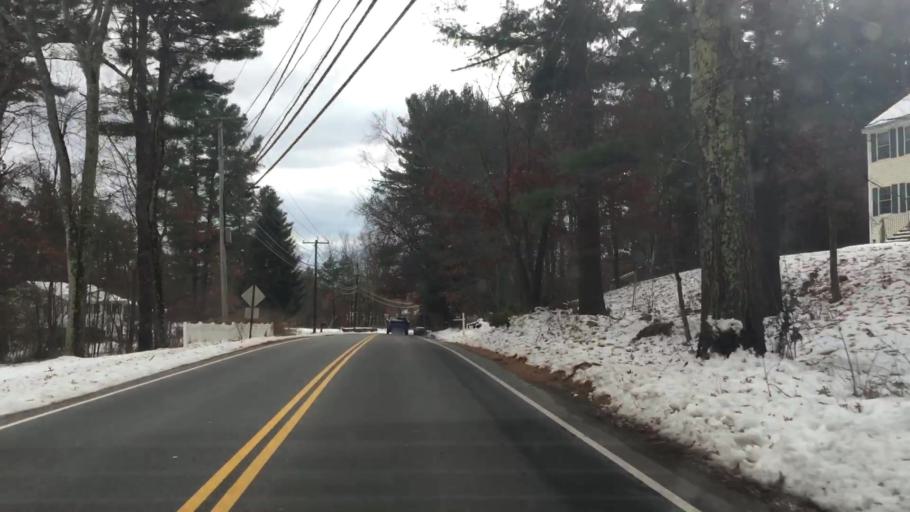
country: US
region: New Hampshire
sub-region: Hillsborough County
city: Pelham
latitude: 42.7145
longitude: -71.3416
